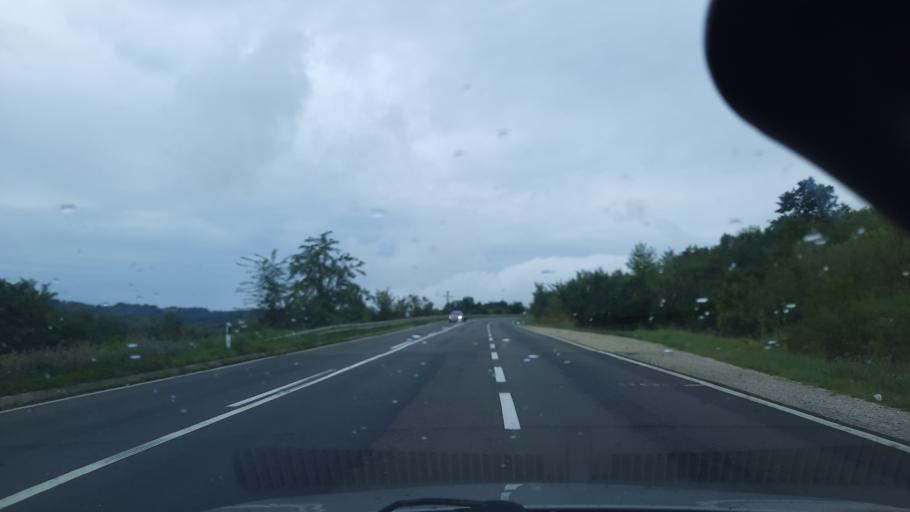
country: RS
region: Central Serbia
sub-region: Sumadijski Okrug
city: Knic
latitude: 43.9521
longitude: 20.8039
